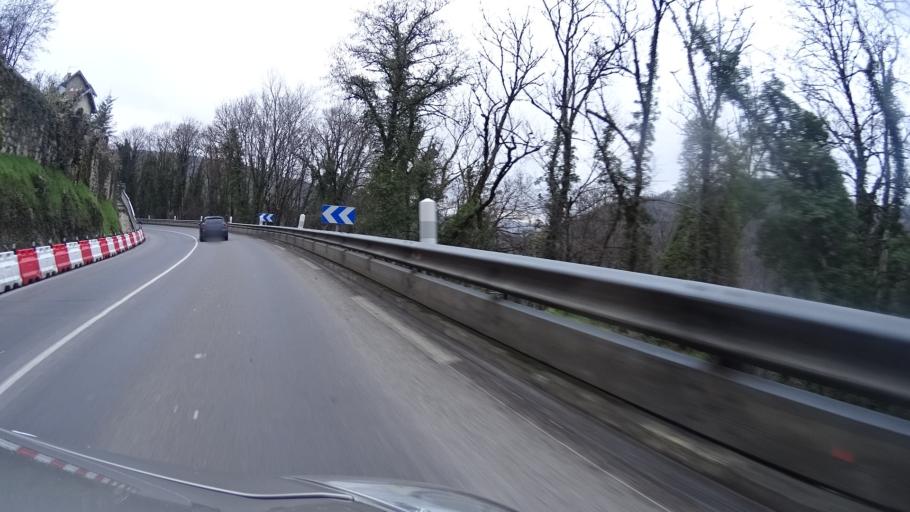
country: FR
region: Franche-Comte
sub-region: Departement du Doubs
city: Morre
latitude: 47.2295
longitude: 6.0621
